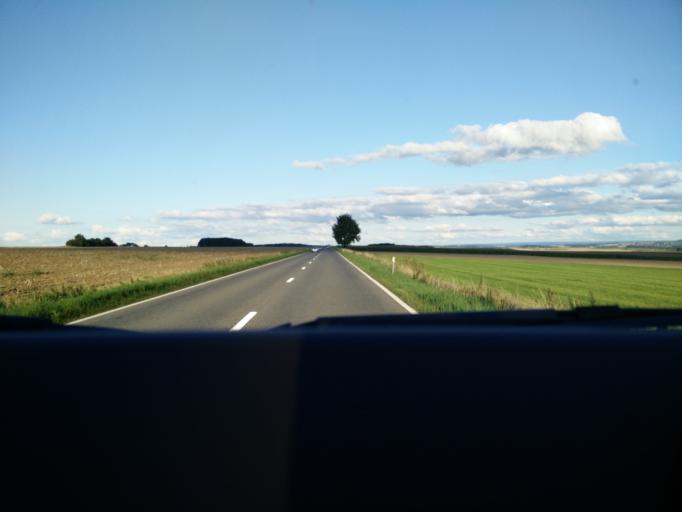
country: BE
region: Wallonia
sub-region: Province de Namur
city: Hastiere-Lavaux
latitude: 50.2408
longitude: 4.7804
